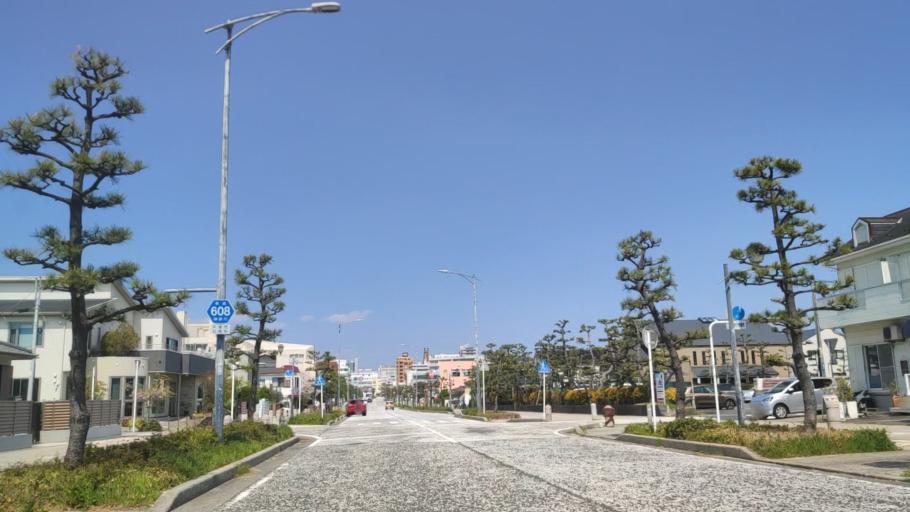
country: JP
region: Kanagawa
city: Hiratsuka
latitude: 35.3209
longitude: 139.3530
